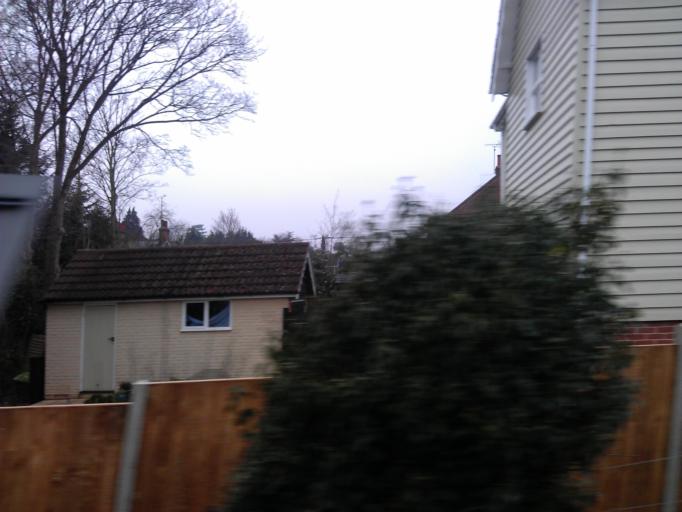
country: GB
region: England
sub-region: Essex
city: Wivenhoe
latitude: 51.8559
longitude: 0.9617
